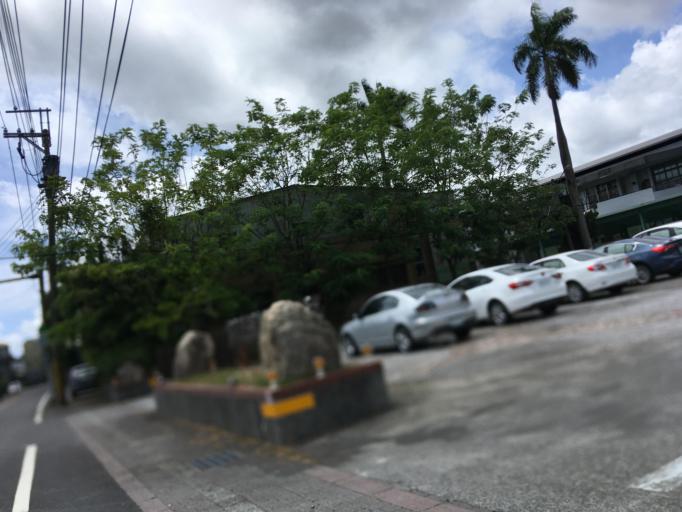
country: TW
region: Taiwan
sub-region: Yilan
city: Yilan
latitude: 24.6936
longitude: 121.7278
